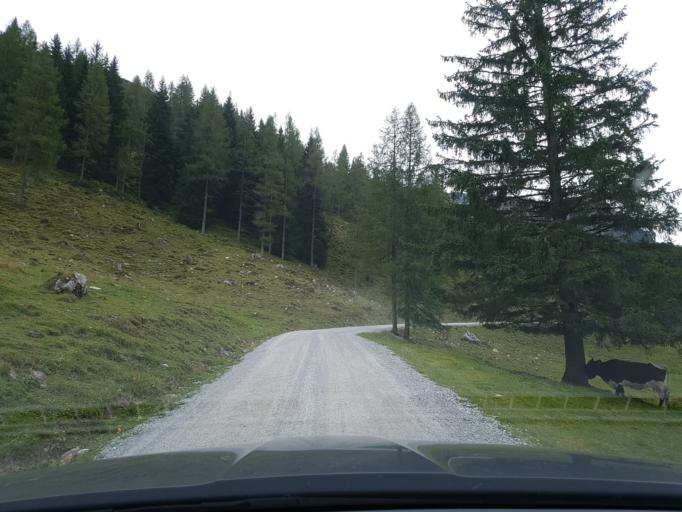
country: AT
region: Salzburg
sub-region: Politischer Bezirk Sankt Johann im Pongau
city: Forstau
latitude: 47.3047
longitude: 13.5820
